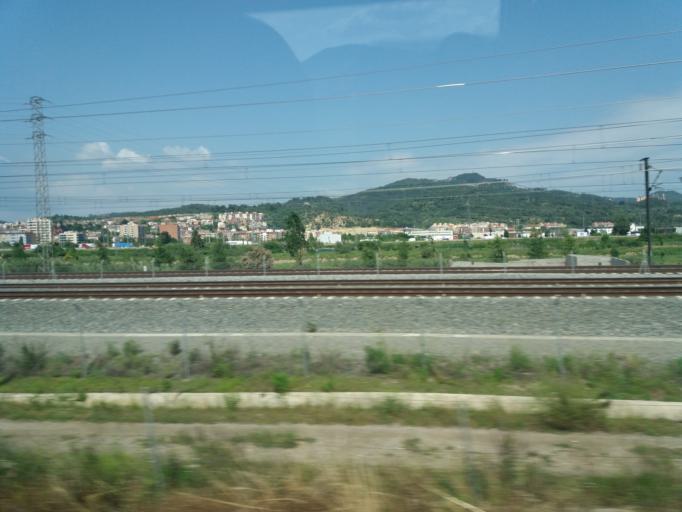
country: ES
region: Catalonia
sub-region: Provincia de Barcelona
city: Sant Vicenc dels Horts
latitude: 41.4015
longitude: 2.0137
